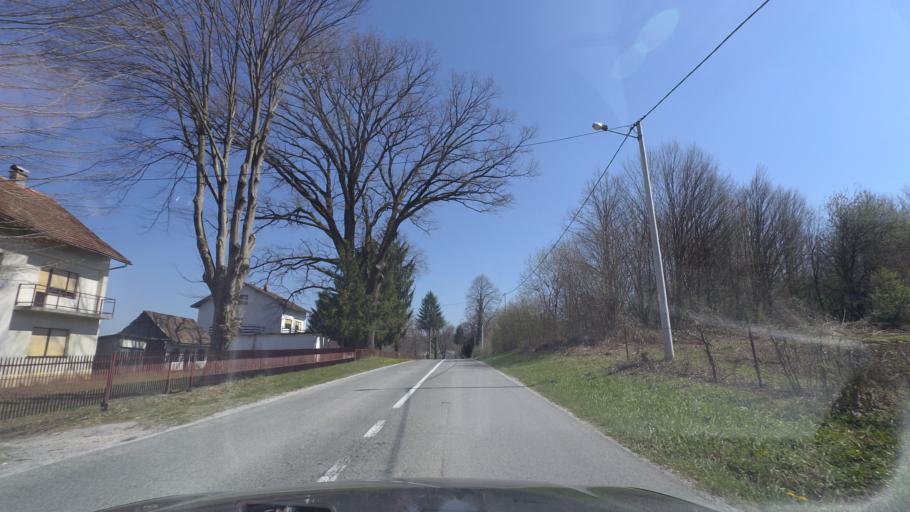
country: HR
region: Sisacko-Moslavacka
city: Gvozd
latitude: 45.3467
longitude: 15.8754
